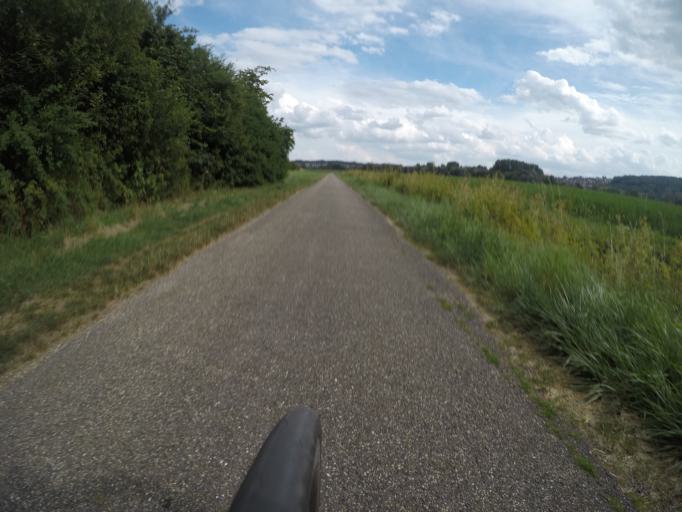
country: DE
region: Baden-Wuerttemberg
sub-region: Regierungsbezirk Stuttgart
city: Weil der Stadt
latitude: 48.7673
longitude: 8.8624
